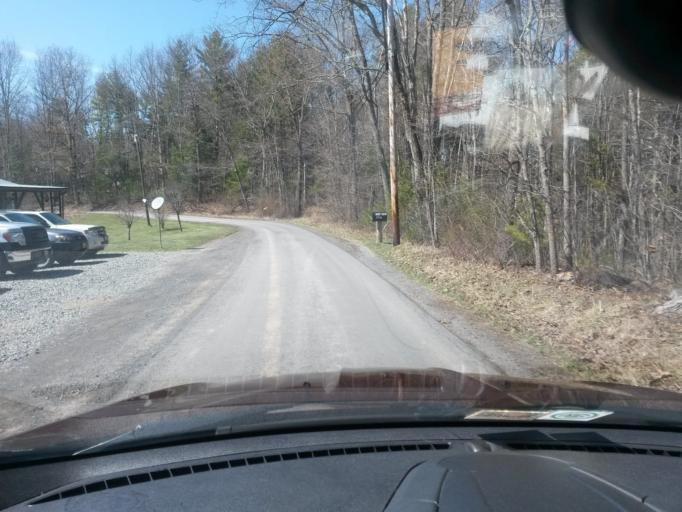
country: US
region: West Virginia
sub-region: Greenbrier County
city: White Sulphur Springs
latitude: 37.6788
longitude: -80.3263
